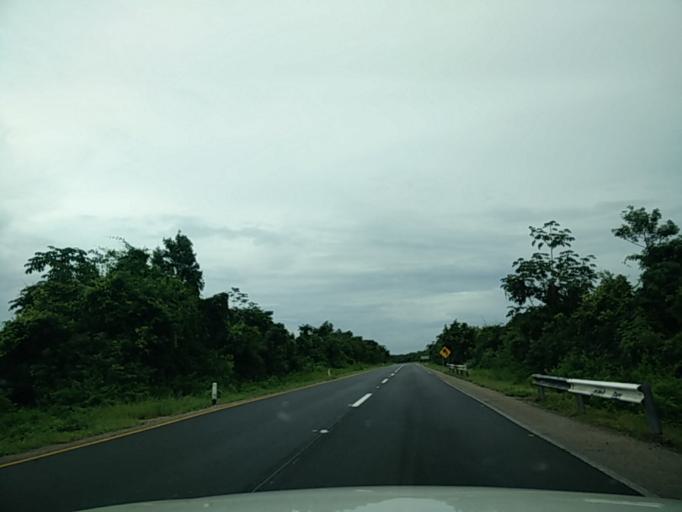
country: MX
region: Quintana Roo
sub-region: Lazaro Cardenas
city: Nuevo Xcan
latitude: 20.8792
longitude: -87.6029
